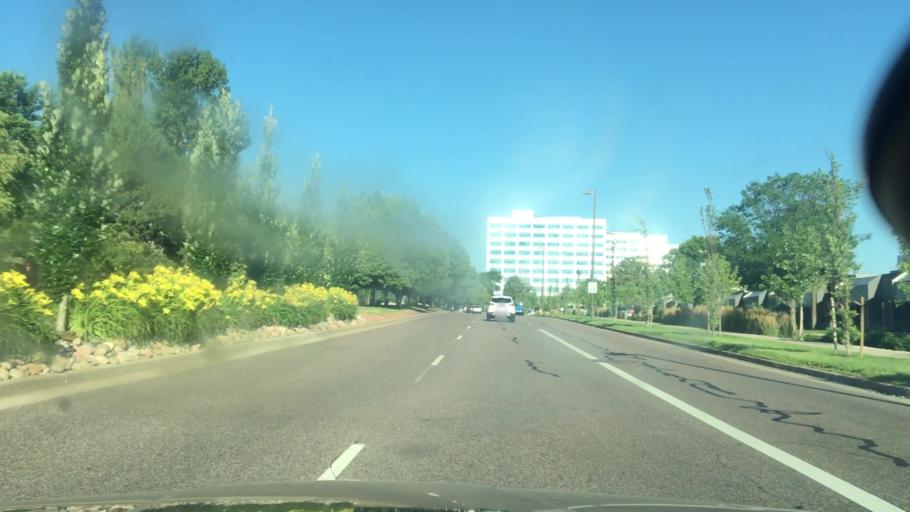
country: US
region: Colorado
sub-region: Arapahoe County
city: Castlewood
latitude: 39.6096
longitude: -104.8861
